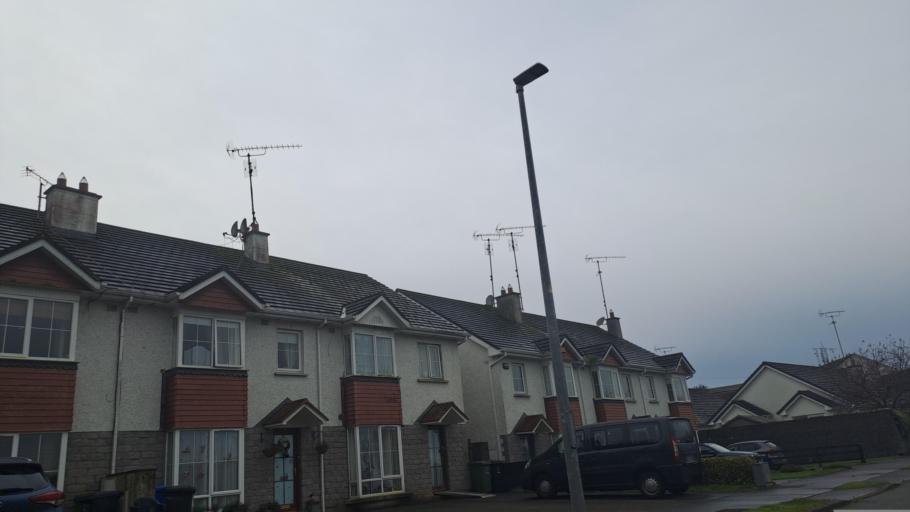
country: IE
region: Ulster
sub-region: An Cabhan
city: Virginia
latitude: 53.8372
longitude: -7.0839
